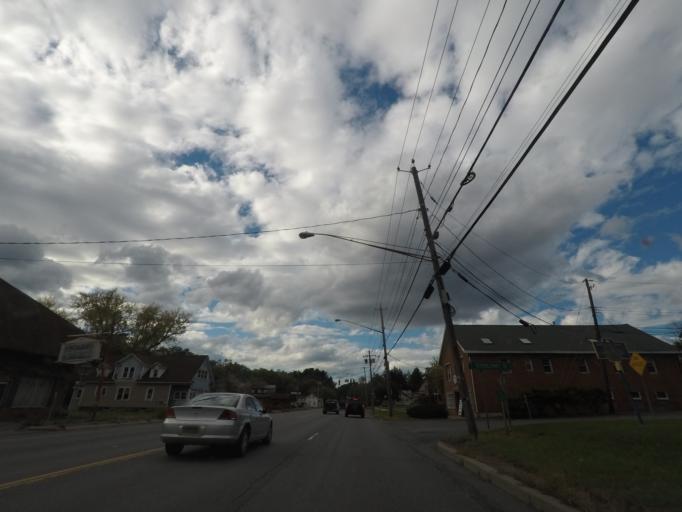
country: US
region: New York
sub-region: Albany County
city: Westmere
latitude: 42.7036
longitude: -73.9098
